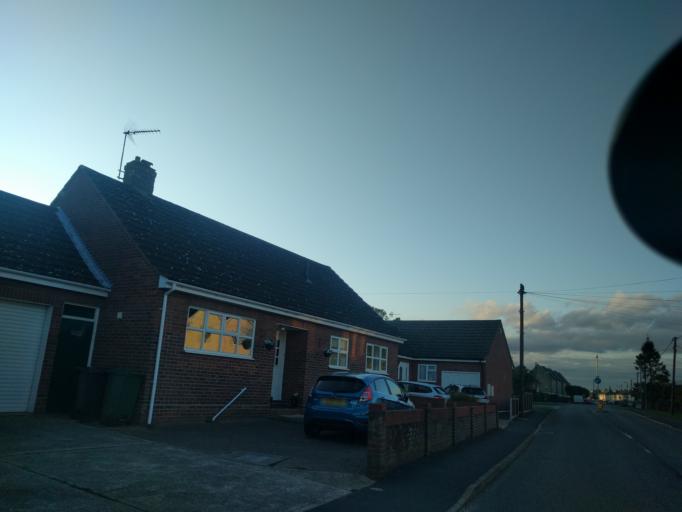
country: GB
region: England
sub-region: Essex
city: Rayne
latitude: 51.8745
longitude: 0.5761
